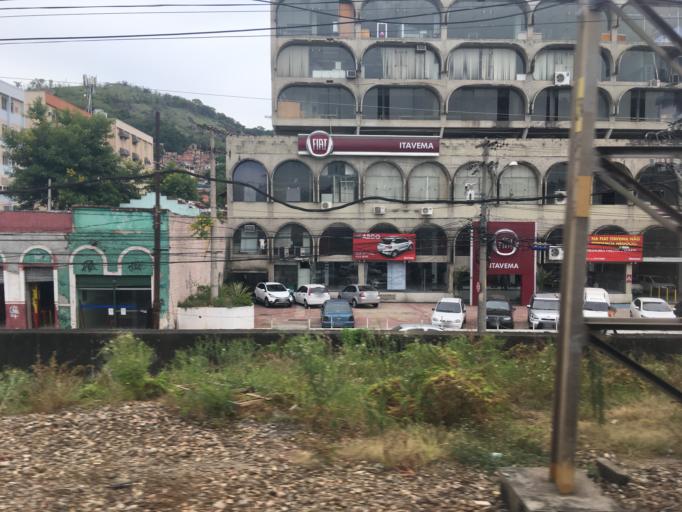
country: BR
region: Rio de Janeiro
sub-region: Rio De Janeiro
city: Rio de Janeiro
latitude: -22.9023
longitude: -43.2659
